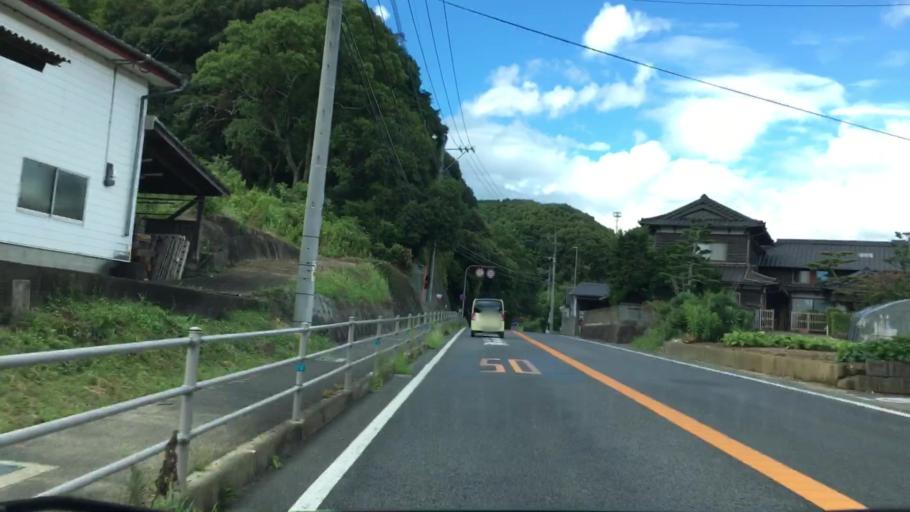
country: JP
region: Nagasaki
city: Sasebo
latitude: 33.1623
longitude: 129.8332
